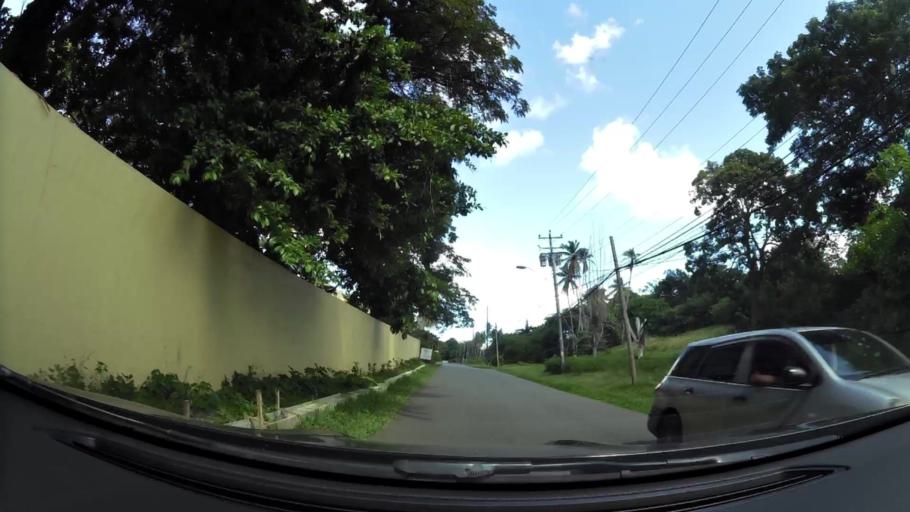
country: TT
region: Tobago
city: Scarborough
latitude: 11.2123
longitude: -60.7785
